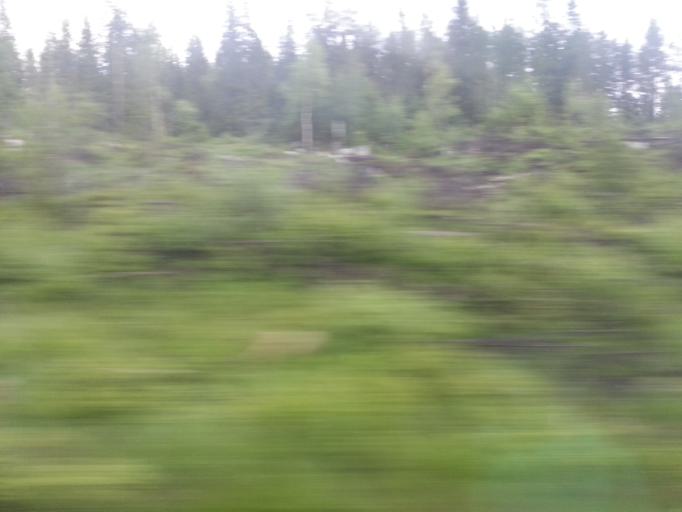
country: NO
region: Sor-Trondelag
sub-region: Rennebu
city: Berkak
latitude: 62.9193
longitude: 10.1473
